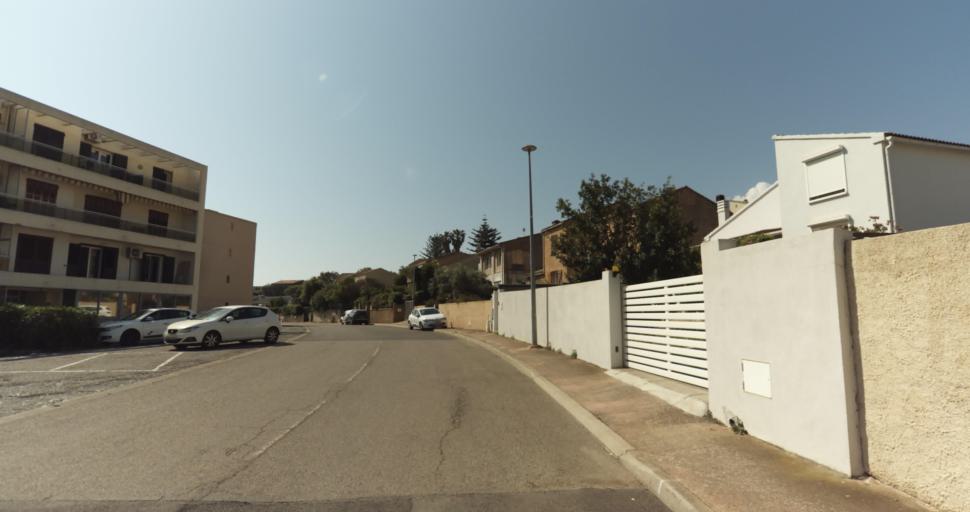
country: FR
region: Corsica
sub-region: Departement de la Haute-Corse
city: Biguglia
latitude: 42.6271
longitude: 9.4295
